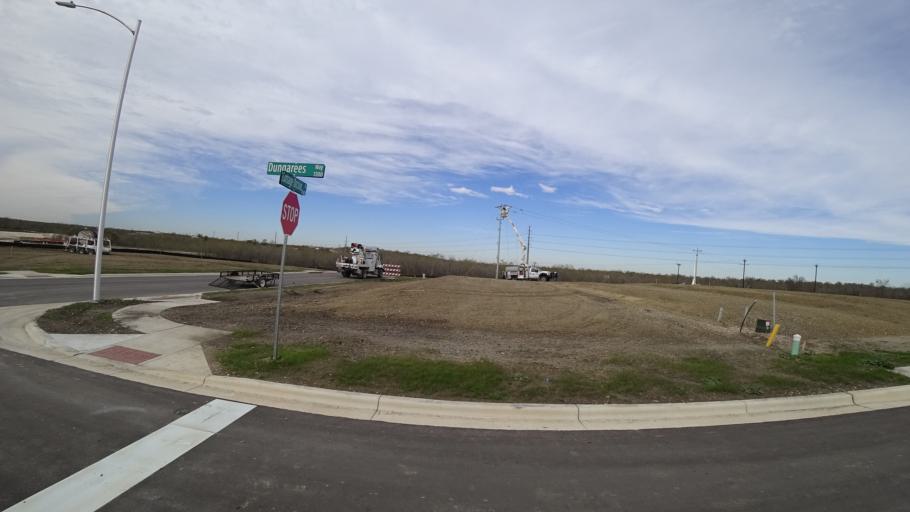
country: US
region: Texas
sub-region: Travis County
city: Garfield
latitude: 30.1520
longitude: -97.5894
